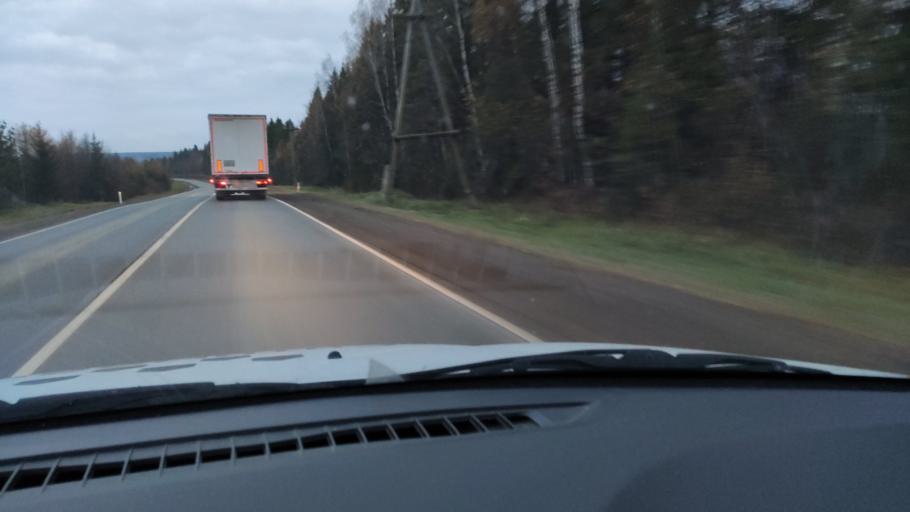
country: RU
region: Kirov
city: Kostino
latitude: 58.8566
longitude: 53.1903
